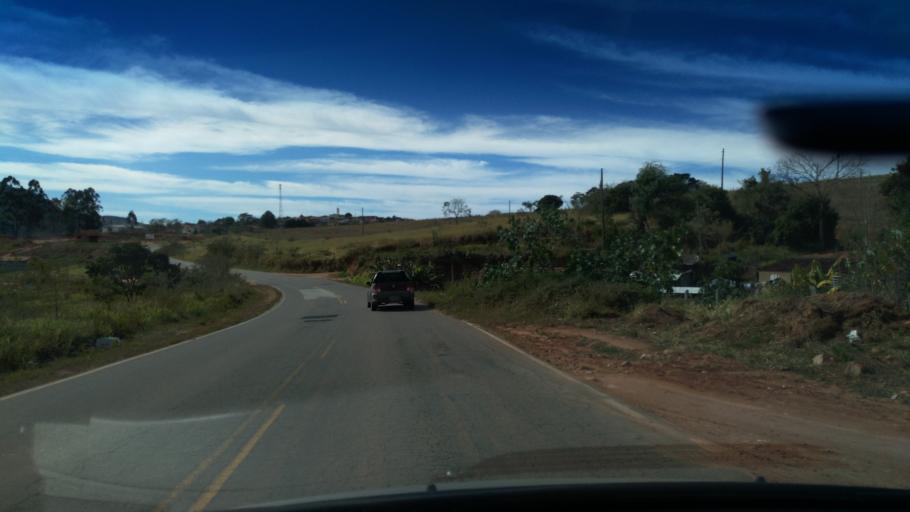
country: BR
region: Minas Gerais
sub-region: Andradas
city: Andradas
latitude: -22.0679
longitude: -46.4511
